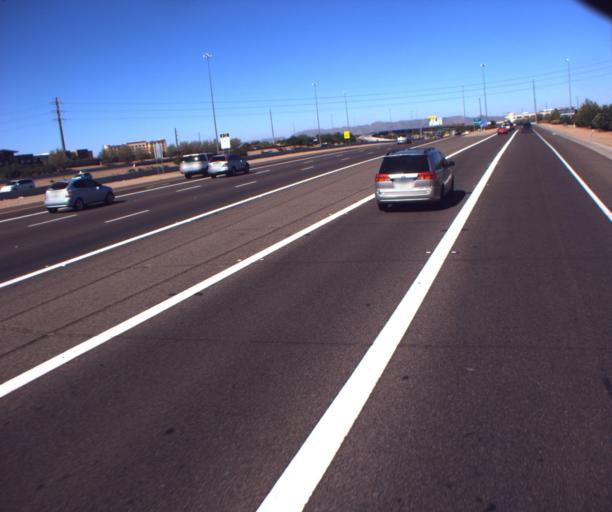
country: US
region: Arizona
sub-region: Maricopa County
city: Chandler
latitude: 33.2893
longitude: -111.8830
